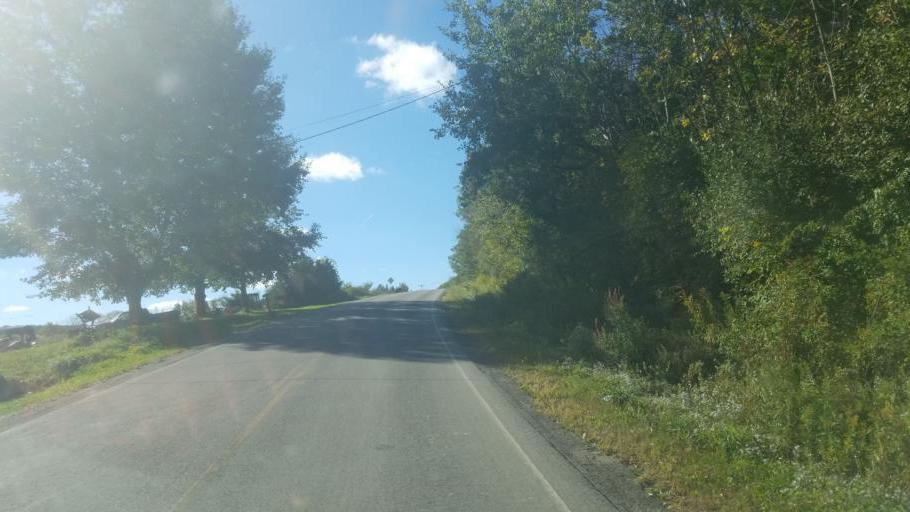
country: US
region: New York
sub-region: Allegany County
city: Friendship
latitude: 42.2760
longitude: -78.1536
